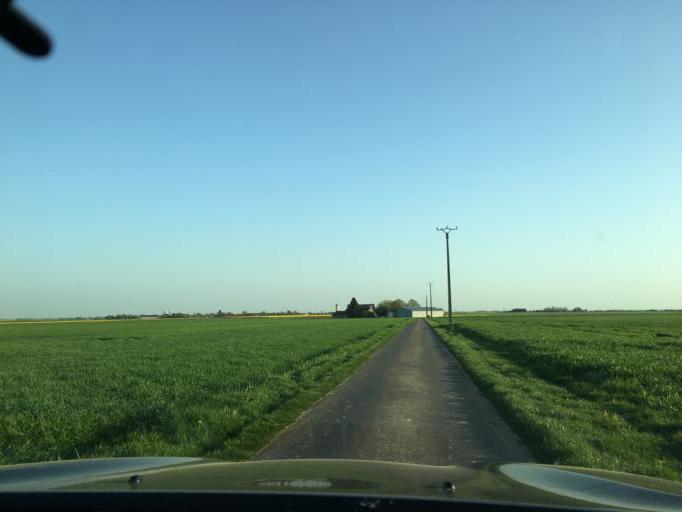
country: FR
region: Centre
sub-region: Departement du Loir-et-Cher
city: Ouzouer-le-Marche
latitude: 47.8204
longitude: 1.5251
